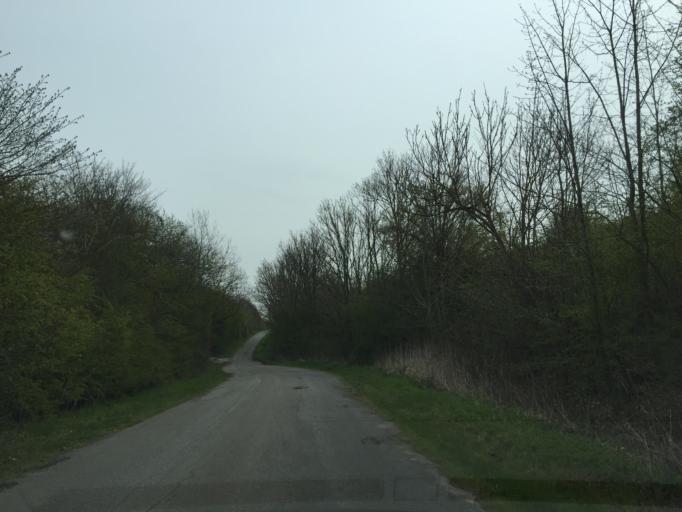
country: DK
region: South Denmark
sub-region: Odense Kommune
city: Neder Holluf
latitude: 55.3905
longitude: 10.4514
